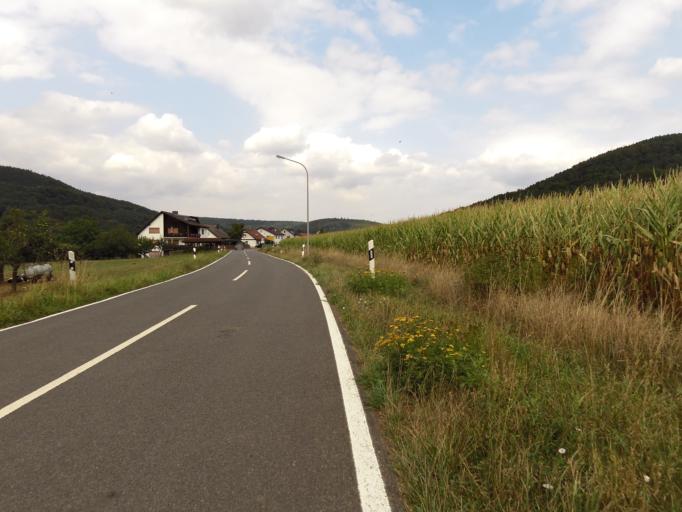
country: DE
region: Hesse
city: Hochst im Odenwald
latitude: 49.8031
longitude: 9.0073
